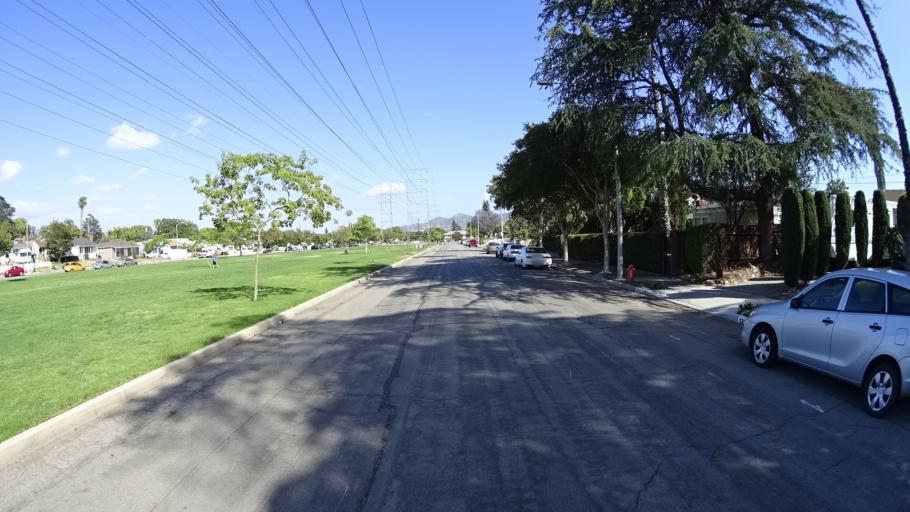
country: US
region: California
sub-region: Los Angeles County
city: North Hollywood
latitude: 34.1712
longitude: -118.3558
